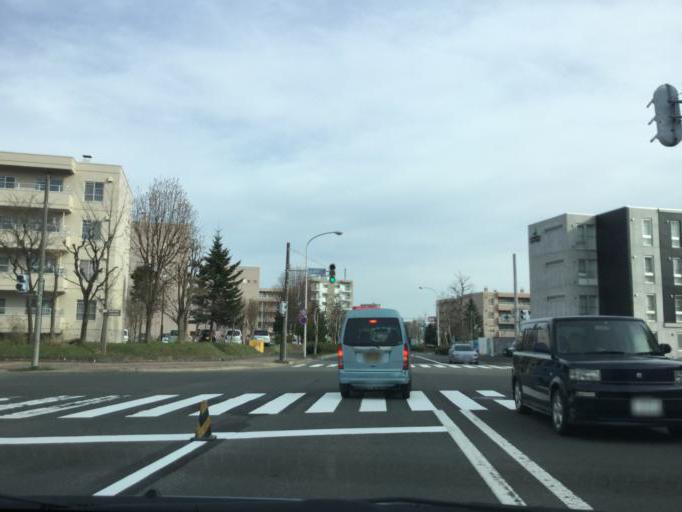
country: JP
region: Hokkaido
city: Ebetsu
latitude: 43.0341
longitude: 141.4657
